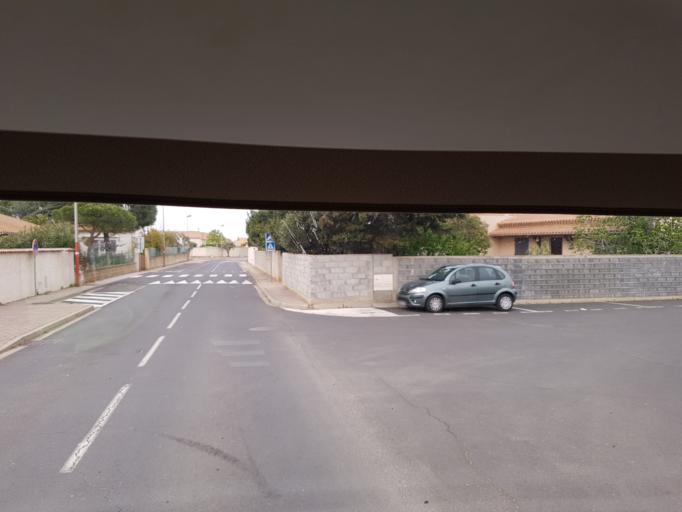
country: FR
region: Languedoc-Roussillon
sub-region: Departement de l'Herault
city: Serignan
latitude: 43.2770
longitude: 3.2709
